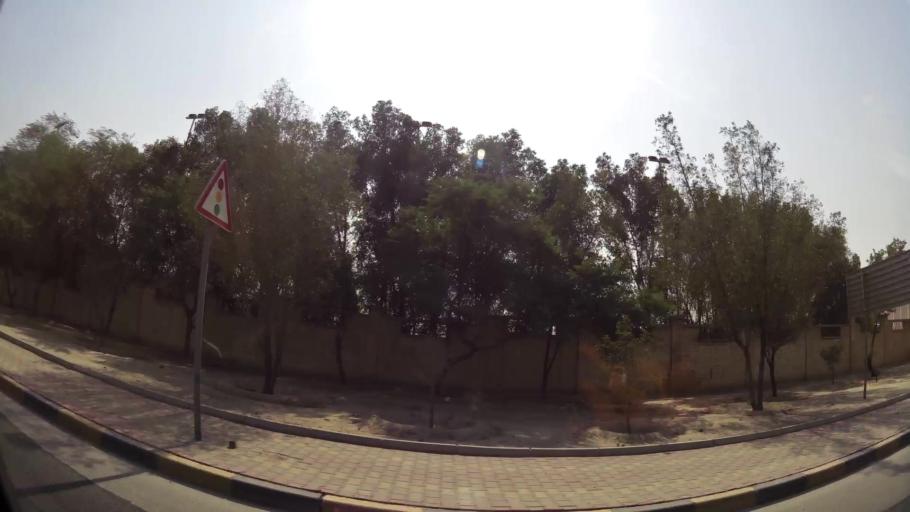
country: KW
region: Al Asimah
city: Ash Shamiyah
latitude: 29.3436
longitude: 47.9701
